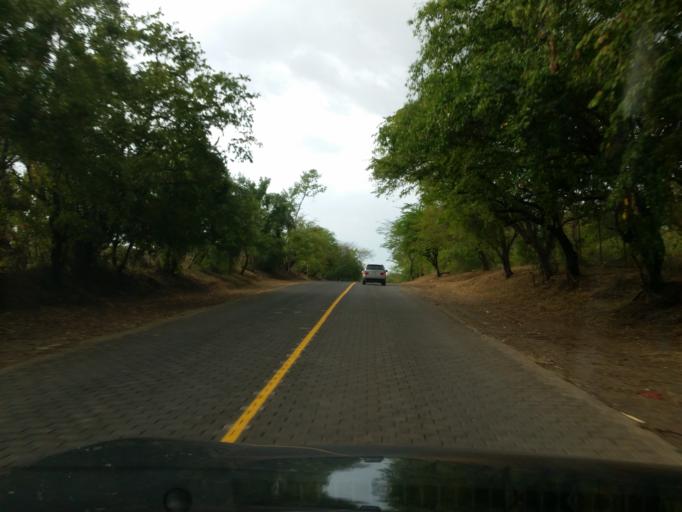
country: NI
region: Managua
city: Carlos Fonseca Amador
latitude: 11.9785
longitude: -86.5150
